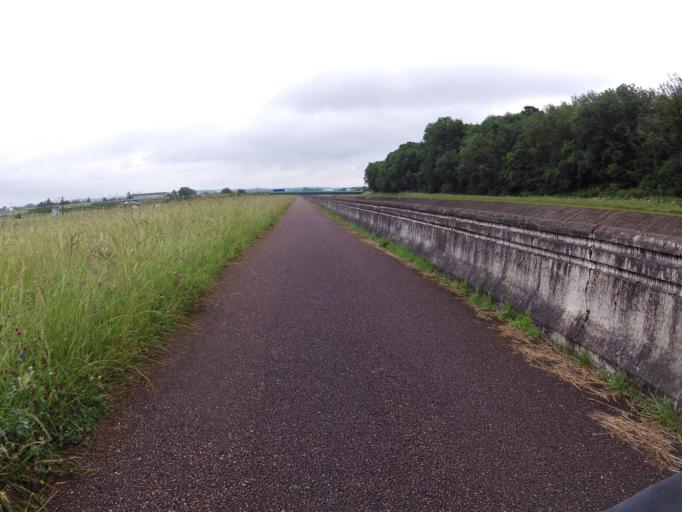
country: FR
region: Champagne-Ardenne
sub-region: Departement de la Haute-Marne
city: Saint-Dizier
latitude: 48.6210
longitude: 4.9338
